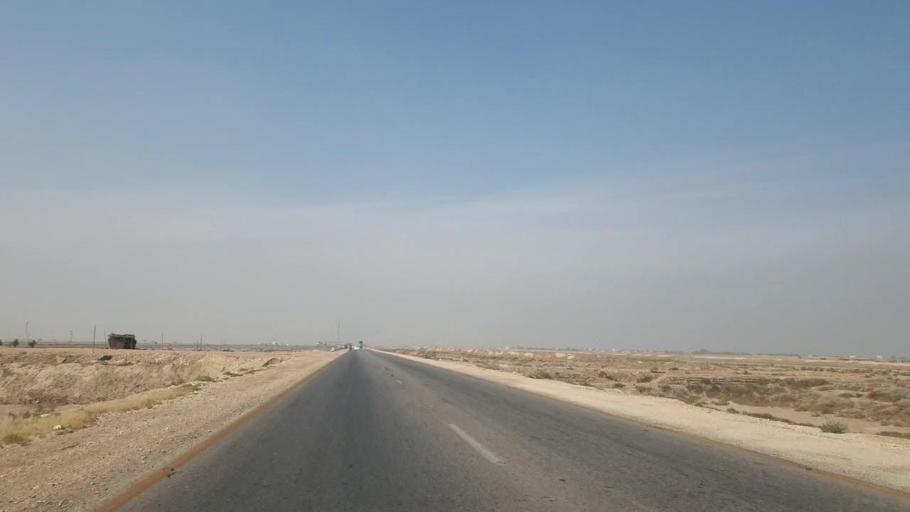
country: PK
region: Sindh
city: Sann
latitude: 25.8907
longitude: 68.2404
